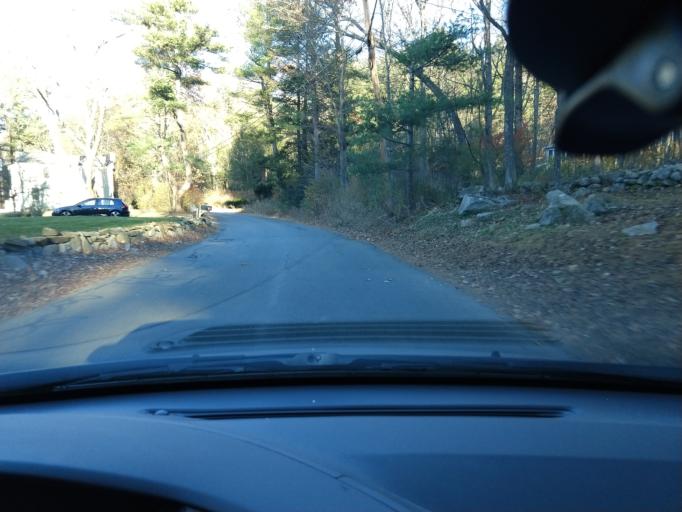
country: US
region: Massachusetts
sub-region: Middlesex County
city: Westford
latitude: 42.5447
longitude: -71.4142
